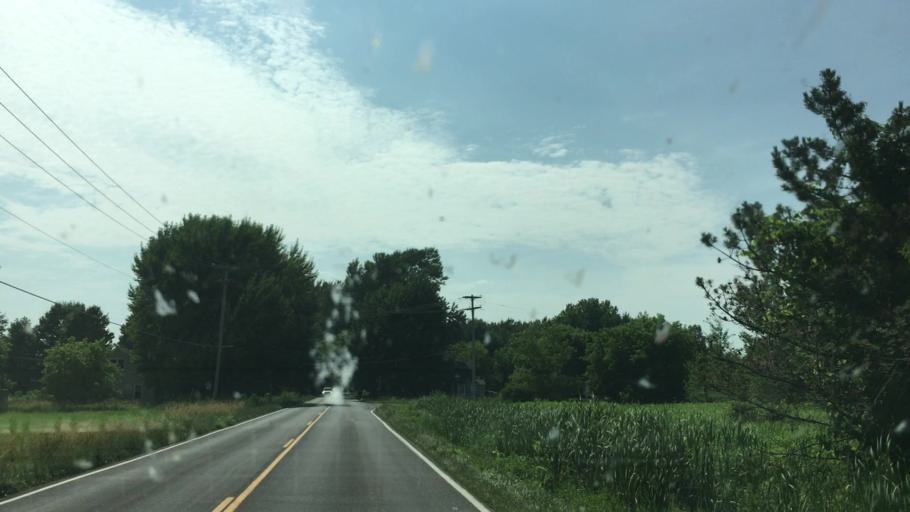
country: US
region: Michigan
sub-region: Kent County
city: Byron Center
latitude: 42.7829
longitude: -85.7119
